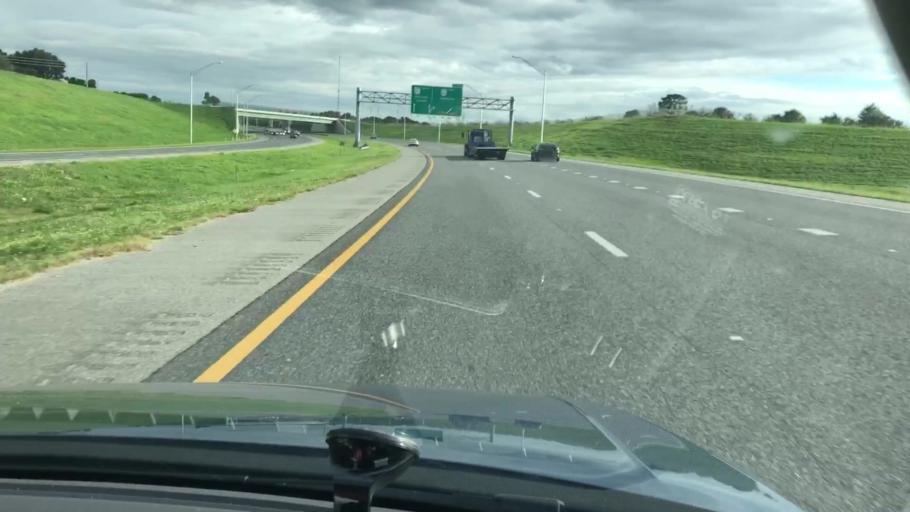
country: US
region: Florida
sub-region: Orange County
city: Paradise Heights
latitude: 28.6624
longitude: -81.5532
